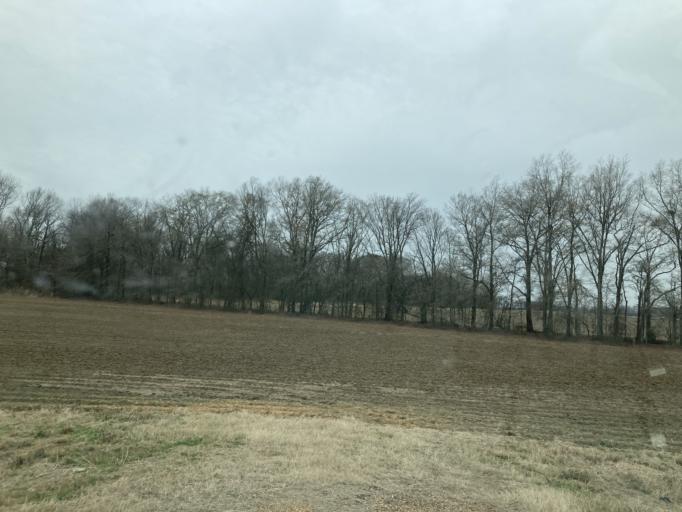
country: US
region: Mississippi
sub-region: Humphreys County
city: Belzoni
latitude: 33.0787
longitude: -90.4807
